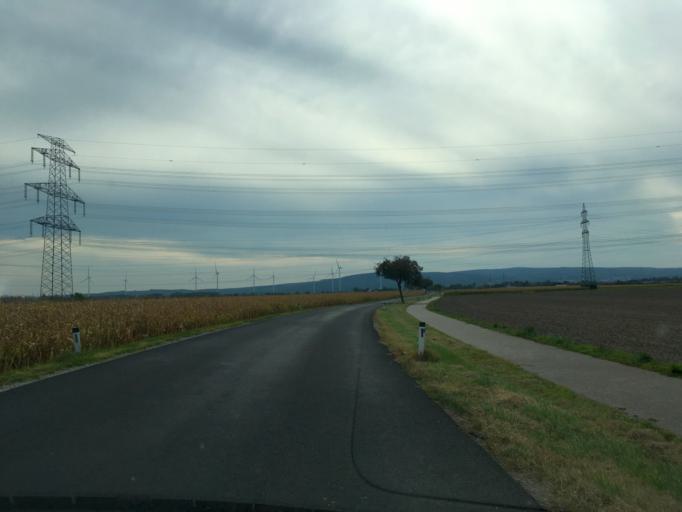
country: AT
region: Lower Austria
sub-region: Politischer Bezirk Bruck an der Leitha
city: Trautmannsdorf an der Leitha
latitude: 48.0323
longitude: 16.6782
